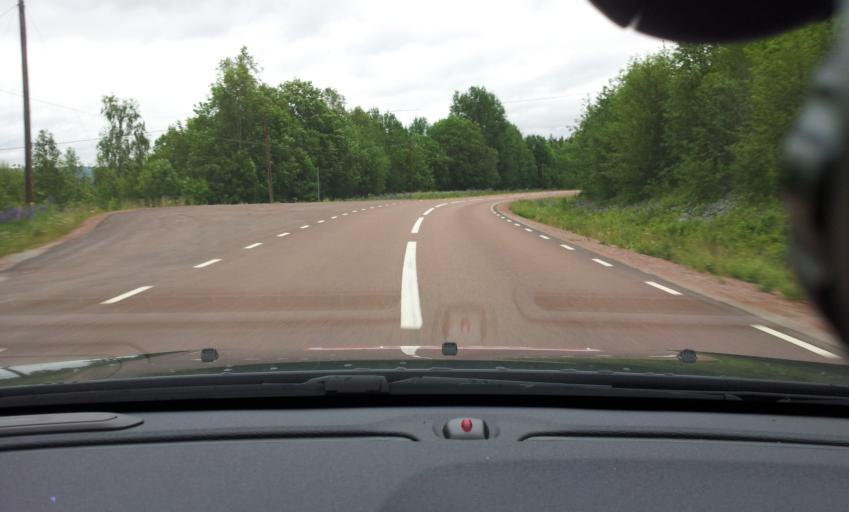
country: SE
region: Jaemtland
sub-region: Ragunda Kommun
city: Hammarstrand
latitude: 63.0284
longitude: 16.5264
